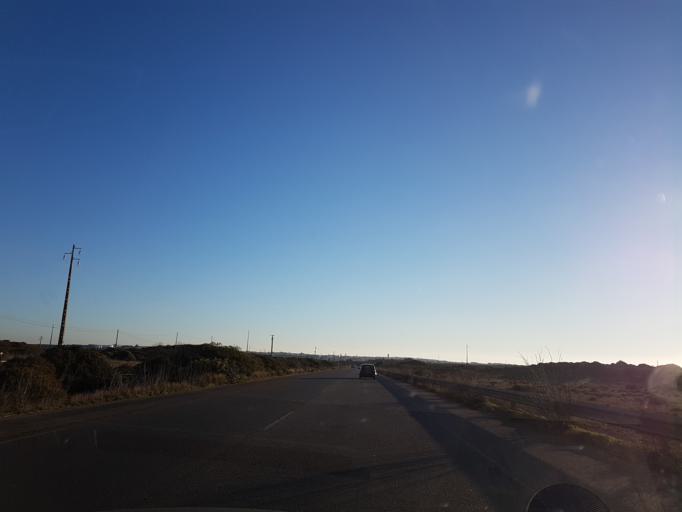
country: PT
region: Faro
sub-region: Vila do Bispo
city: Sagres
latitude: 37.0294
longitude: -8.9365
